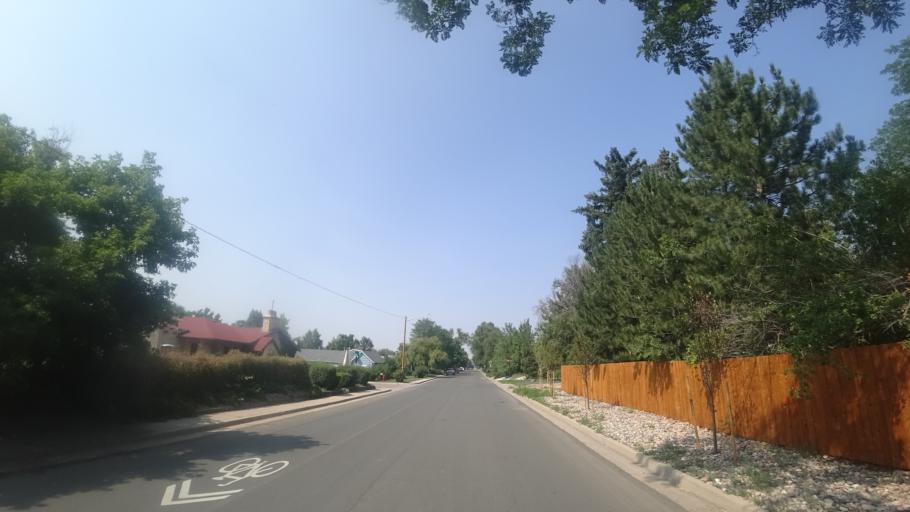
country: US
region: Colorado
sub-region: Arapahoe County
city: Englewood
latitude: 39.6363
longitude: -104.9785
